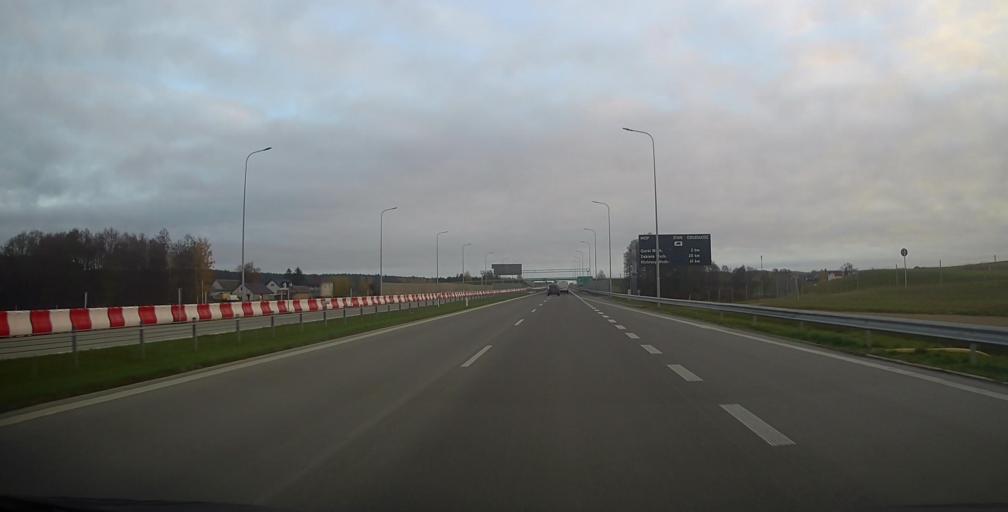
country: PL
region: Podlasie
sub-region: Powiat lomzynski
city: Piatnica
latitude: 53.2515
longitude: 22.1074
